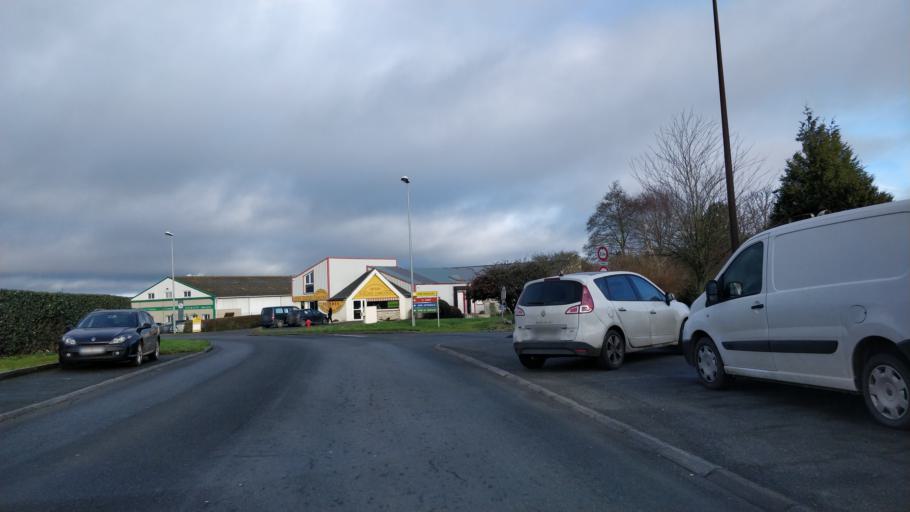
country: FR
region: Brittany
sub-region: Departement des Cotes-d'Armor
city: Lamballe
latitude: 48.4605
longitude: -2.5316
